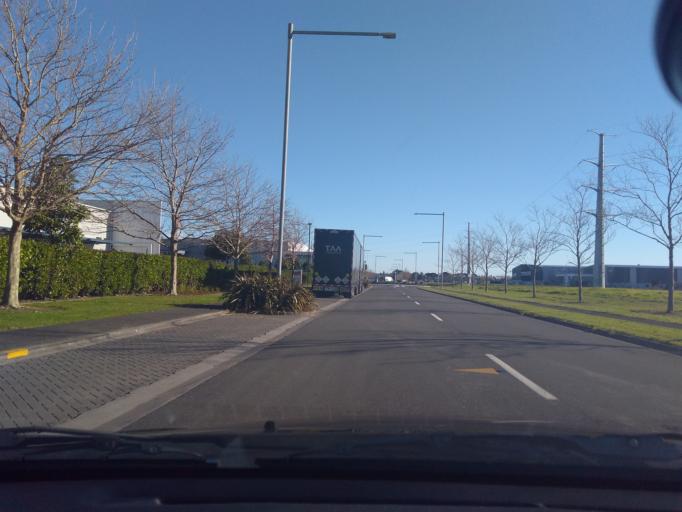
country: NZ
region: Auckland
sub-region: Auckland
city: Tamaki
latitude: -36.9292
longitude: 174.8754
